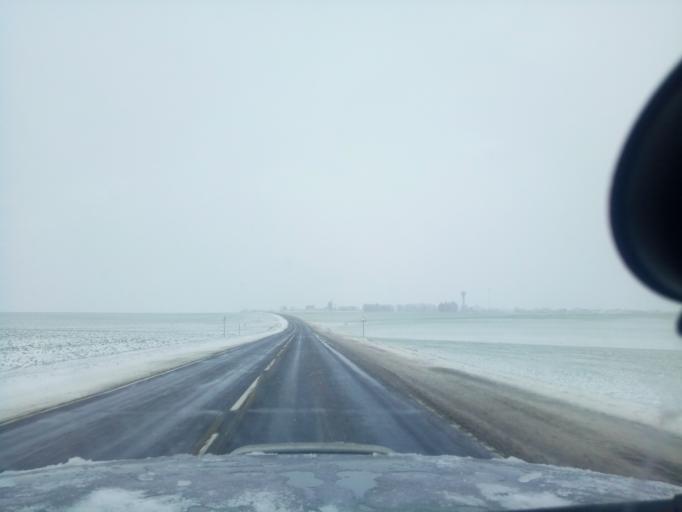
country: BY
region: Minsk
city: Haradzyeya
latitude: 53.3260
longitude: 26.5522
